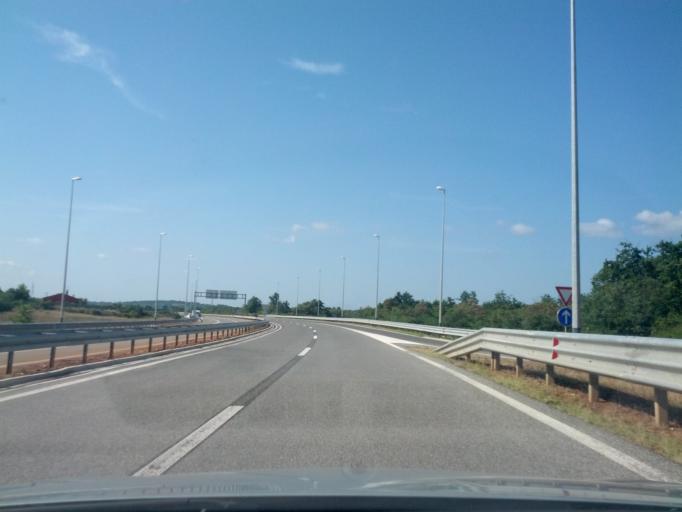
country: SI
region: Piran-Pirano
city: Seca
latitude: 45.4513
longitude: 13.6181
